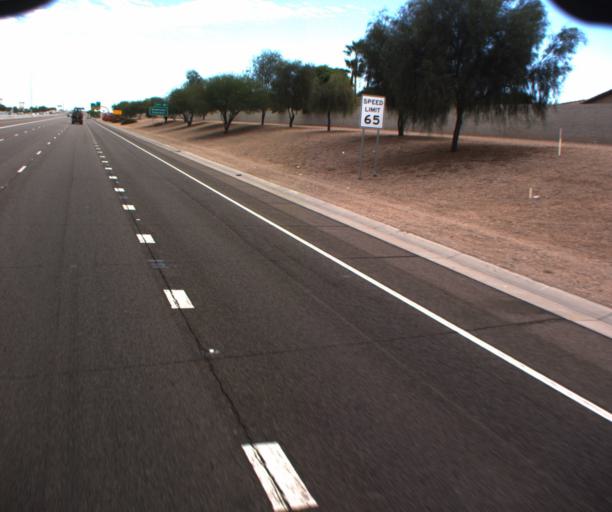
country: US
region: Arizona
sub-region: Maricopa County
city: Chandler
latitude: 33.2871
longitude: -111.8510
